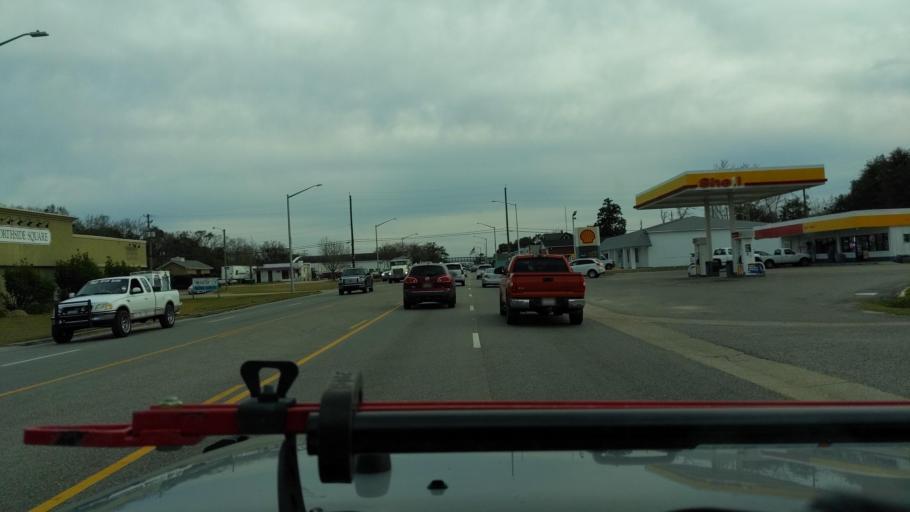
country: US
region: Alabama
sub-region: Baldwin County
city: Foley
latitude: 30.4128
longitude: -87.6839
